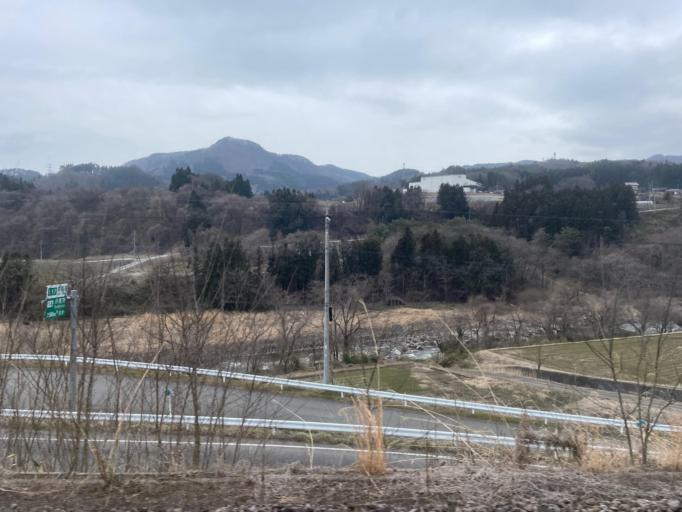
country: JP
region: Gunma
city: Numata
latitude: 36.7018
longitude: 138.9821
